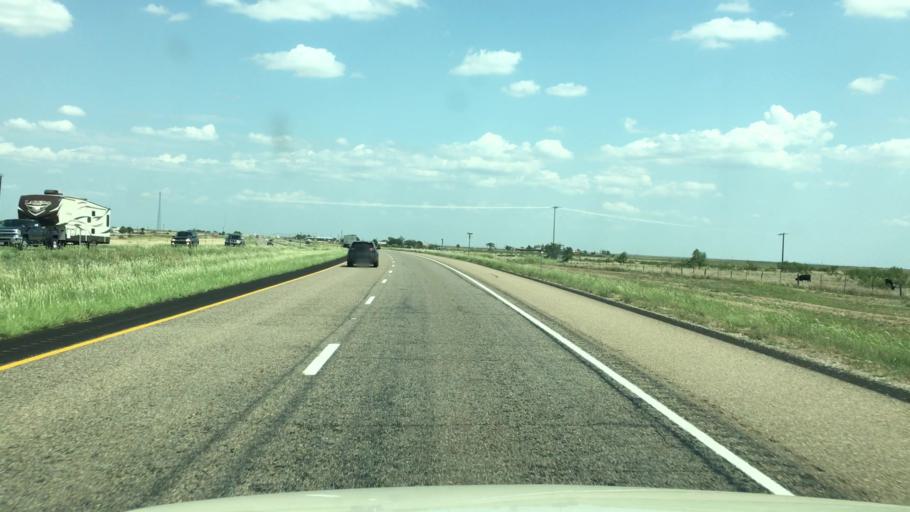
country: US
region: Texas
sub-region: Armstrong County
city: Claude
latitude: 35.0347
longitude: -101.1966
